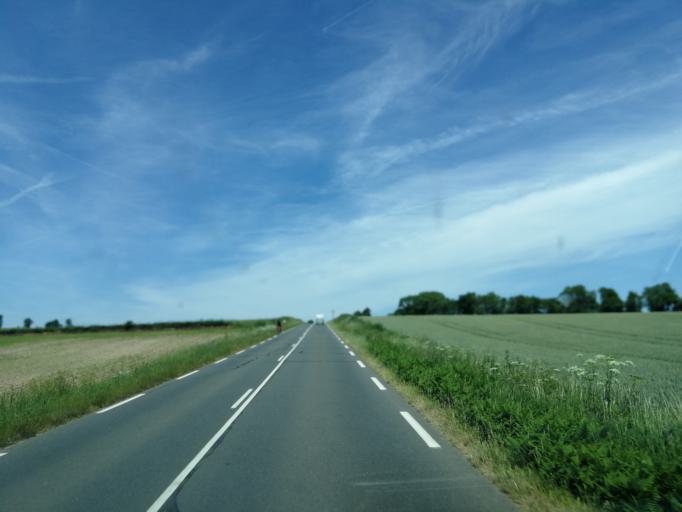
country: FR
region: Pays de la Loire
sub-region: Departement de la Vendee
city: La Tardiere
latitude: 46.6766
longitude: -0.7175
